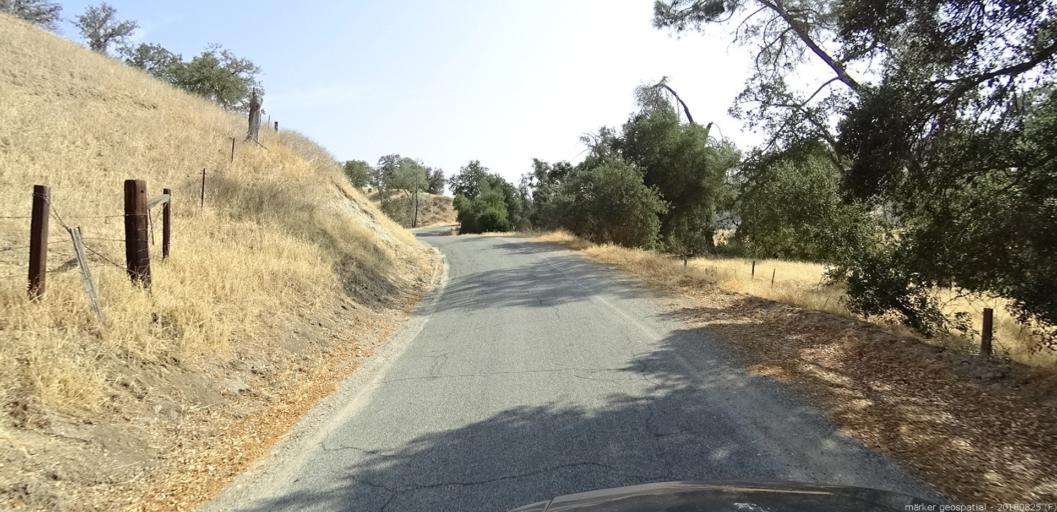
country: US
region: California
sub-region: San Luis Obispo County
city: San Miguel
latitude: 35.8176
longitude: -120.5200
